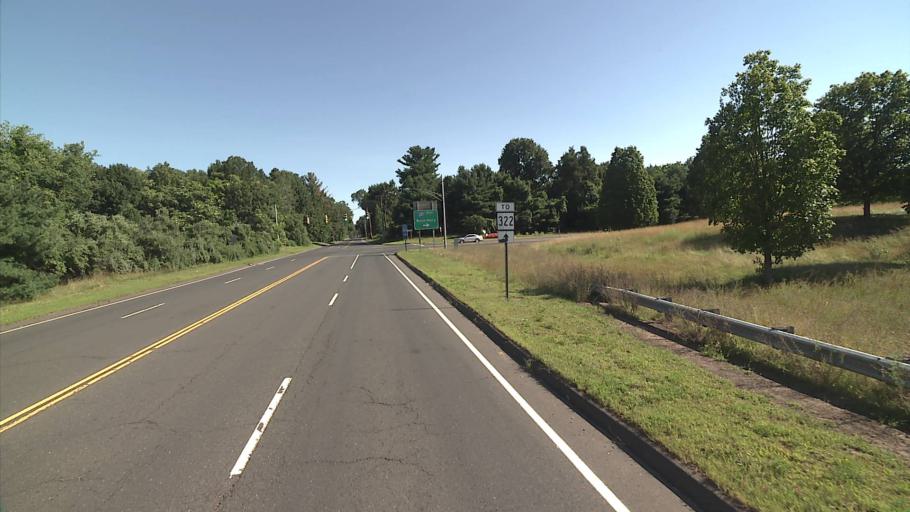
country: US
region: Connecticut
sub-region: New Haven County
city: Cheshire Village
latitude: 41.5579
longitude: -72.8904
